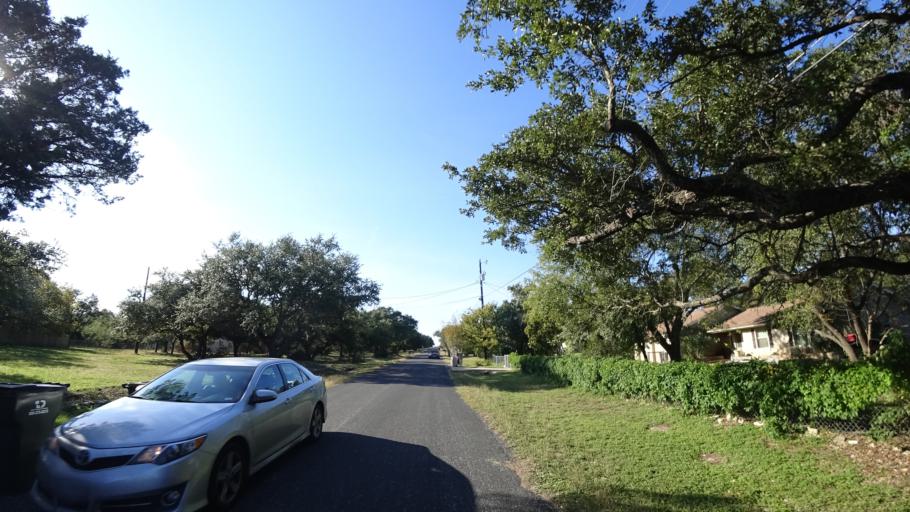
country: US
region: Texas
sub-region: Travis County
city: Barton Creek
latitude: 30.2453
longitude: -97.9082
